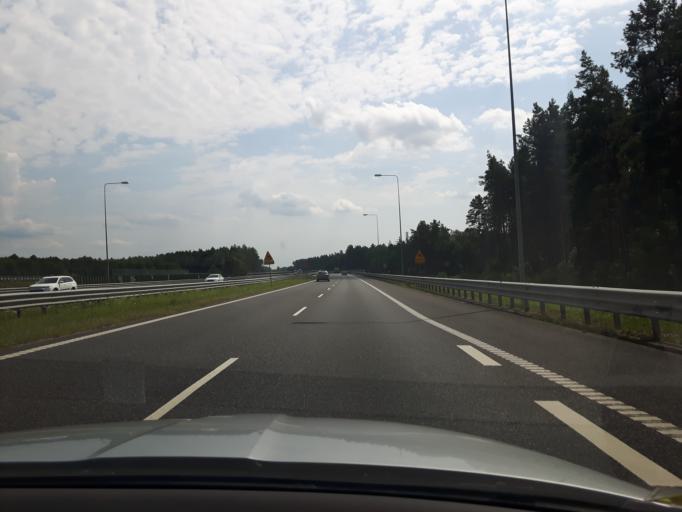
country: PL
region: Warmian-Masurian Voivodeship
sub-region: Powiat olsztynski
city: Olsztynek
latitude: 53.5282
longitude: 20.2794
